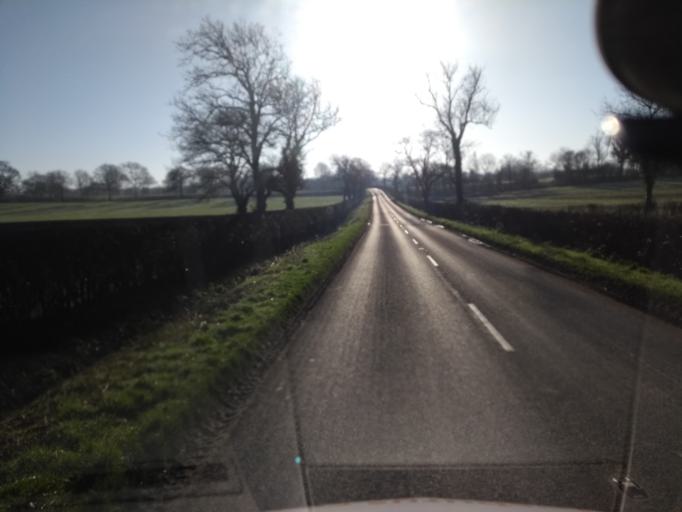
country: GB
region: England
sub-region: Somerset
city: Wincanton
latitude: 51.0728
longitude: -2.3769
